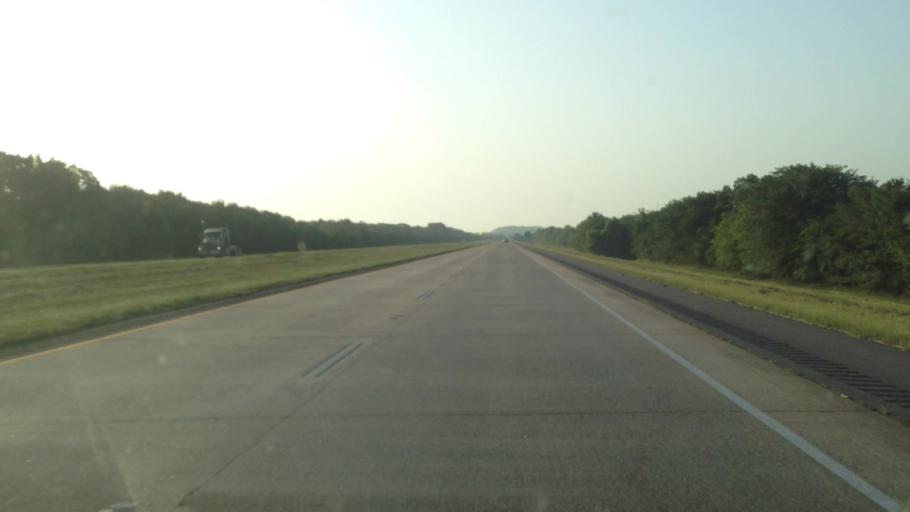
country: US
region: Louisiana
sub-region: Grant Parish
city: Colfax
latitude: 31.5074
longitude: -92.8877
